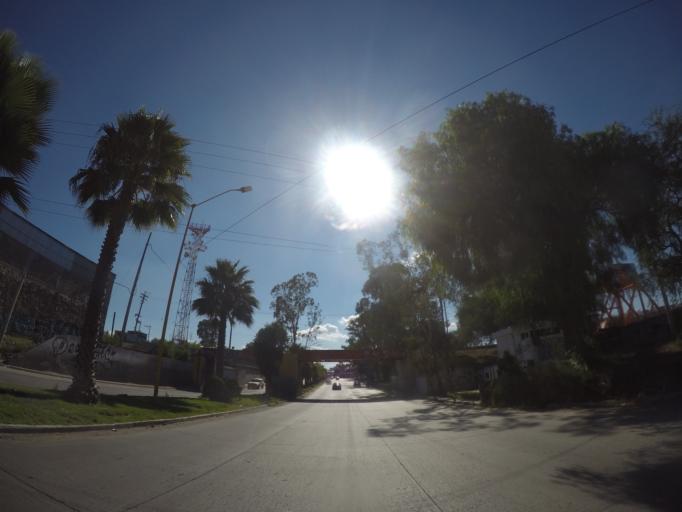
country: MX
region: San Luis Potosi
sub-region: San Luis Potosi
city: San Luis Potosi
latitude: 22.1712
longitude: -100.9673
